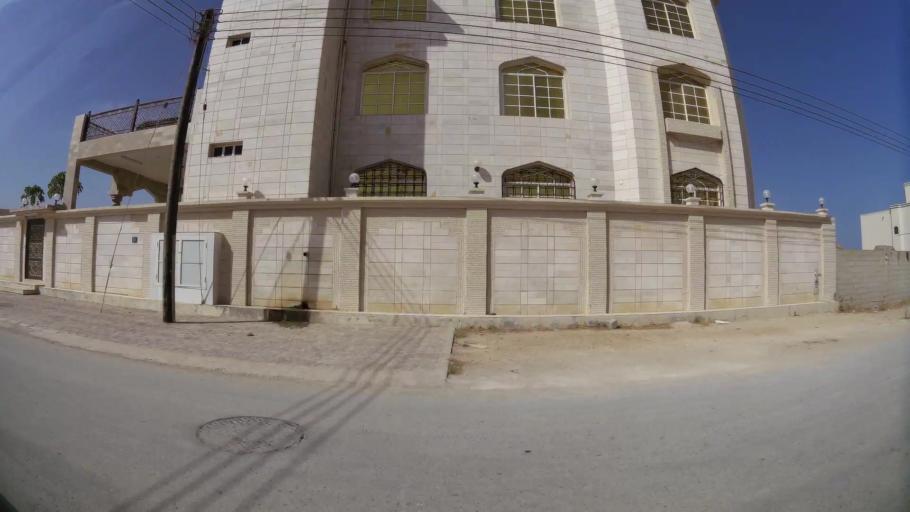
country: OM
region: Zufar
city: Salalah
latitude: 17.0009
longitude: 54.0149
